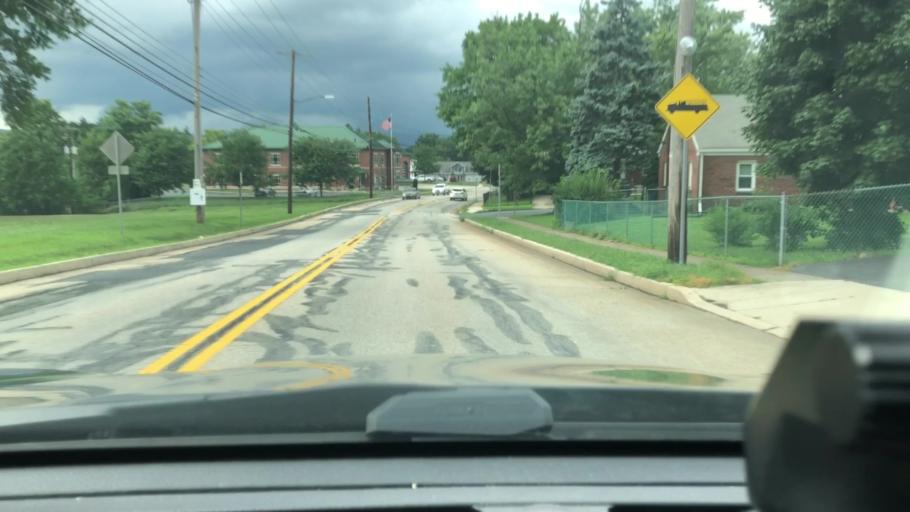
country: US
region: Pennsylvania
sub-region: Dauphin County
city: Colonial Park
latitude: 40.2966
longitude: -76.8108
